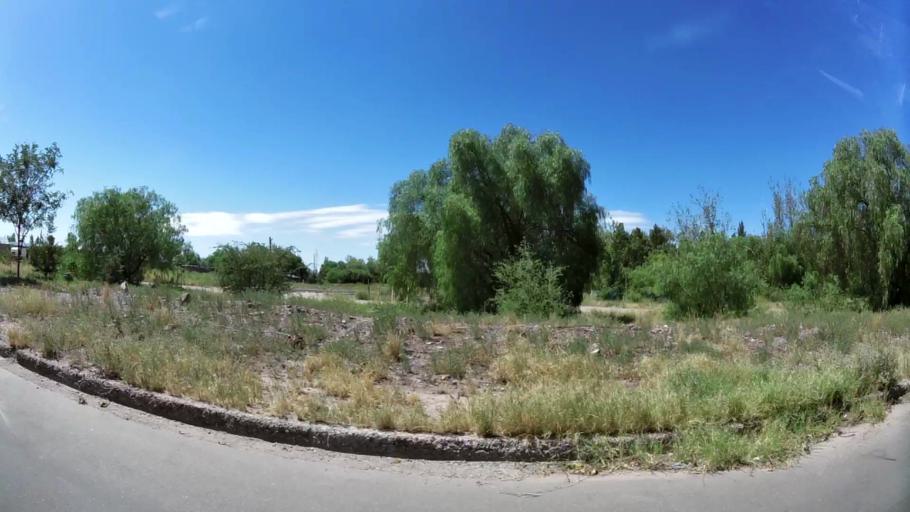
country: AR
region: Mendoza
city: Las Heras
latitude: -32.8399
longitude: -68.8624
